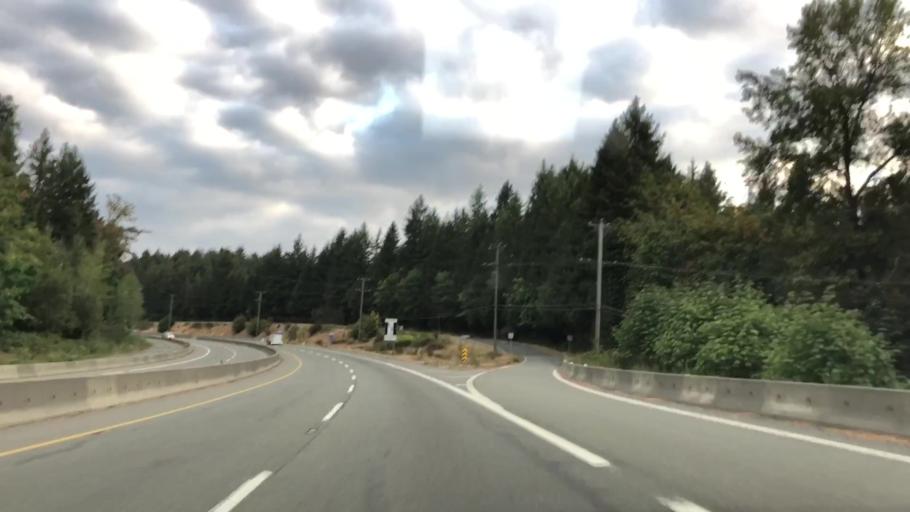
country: CA
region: British Columbia
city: North Cowichan
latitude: 48.8818
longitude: -123.7020
